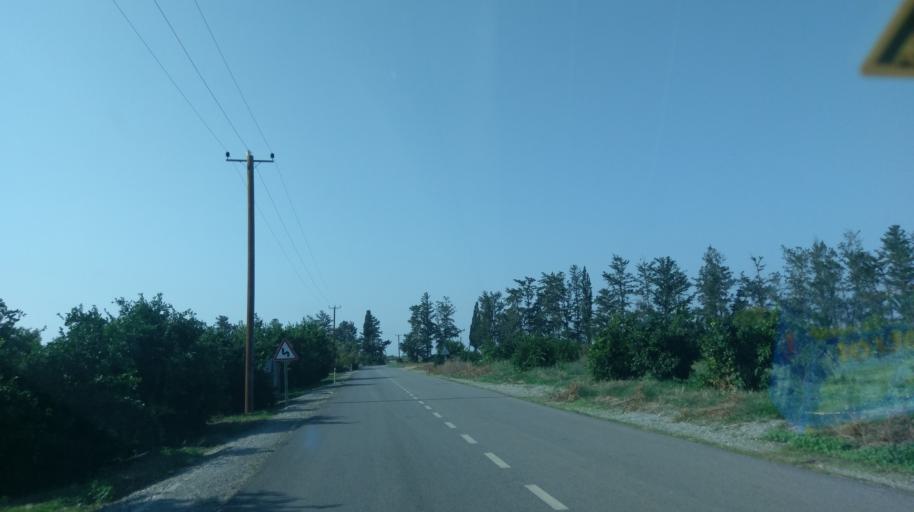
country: CY
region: Lefkosia
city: Morfou
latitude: 35.2099
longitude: 32.9704
